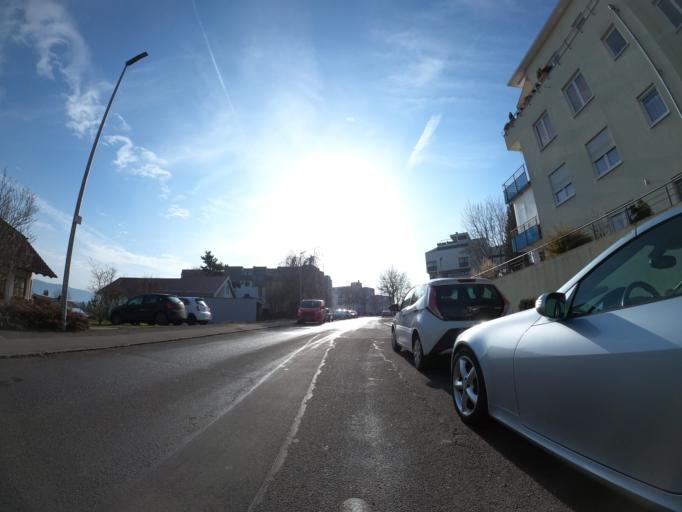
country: DE
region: Baden-Wuerttemberg
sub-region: Tuebingen Region
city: Metzingen
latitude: 48.5404
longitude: 9.2727
